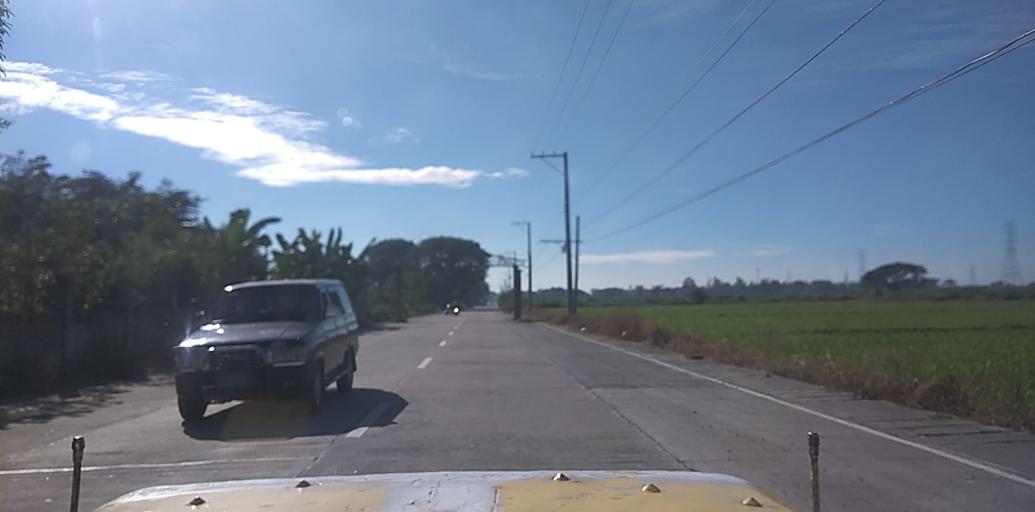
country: PH
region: Central Luzon
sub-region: Province of Pampanga
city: Anao
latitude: 15.1312
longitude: 120.6969
